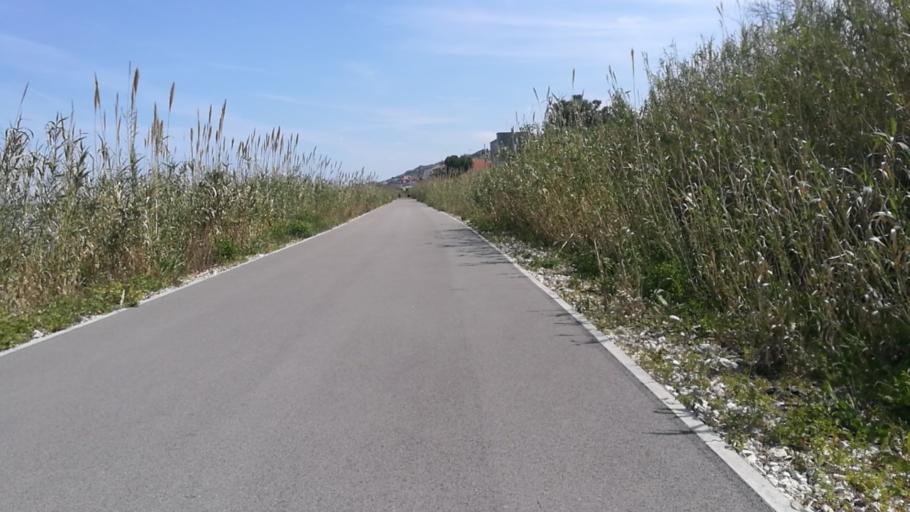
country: IT
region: Abruzzo
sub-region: Provincia di Chieti
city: Marina di San Vito
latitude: 42.3142
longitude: 14.4384
